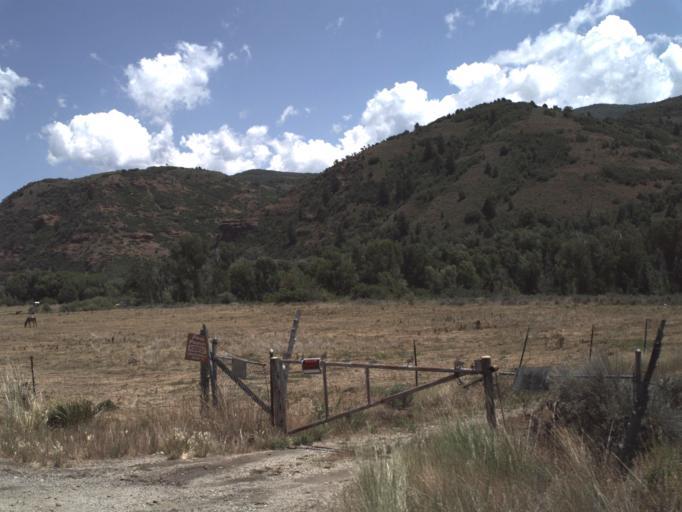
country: US
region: Utah
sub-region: Weber County
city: Wolf Creek
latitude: 41.2932
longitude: -111.6321
